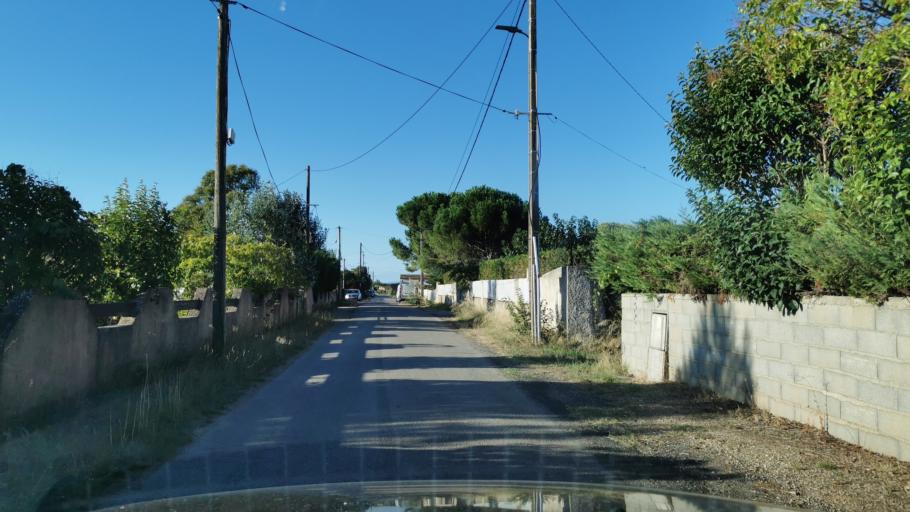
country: FR
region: Languedoc-Roussillon
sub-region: Departement de l'Aude
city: Coursan
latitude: 43.2610
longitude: 3.0223
